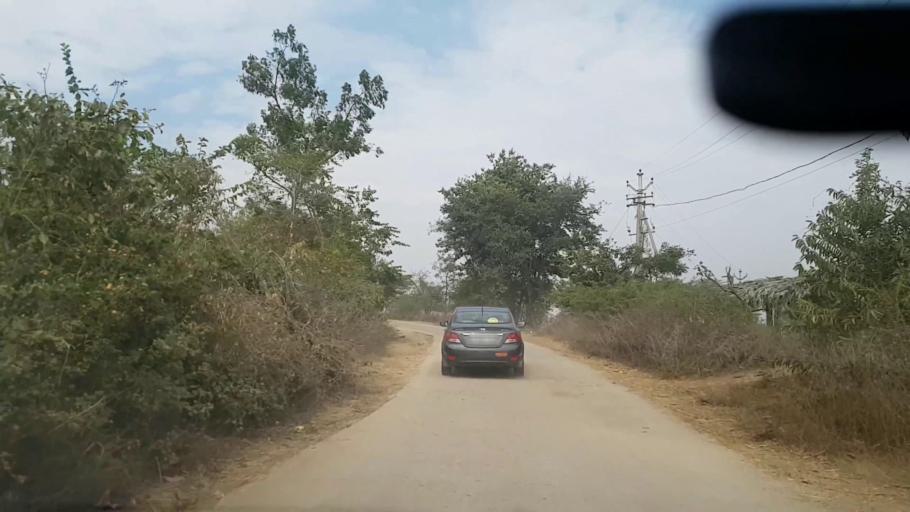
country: IN
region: Telangana
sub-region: Rangareddi
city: Lal Bahadur Nagar
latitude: 17.1631
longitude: 78.7875
